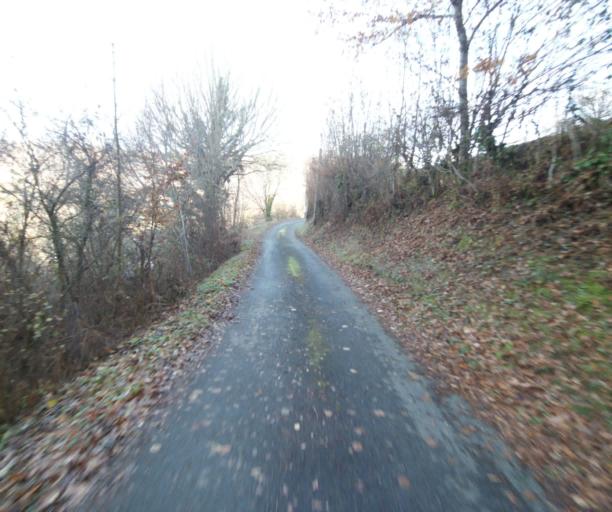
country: FR
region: Limousin
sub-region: Departement de la Correze
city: Laguenne
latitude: 45.2466
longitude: 1.7867
